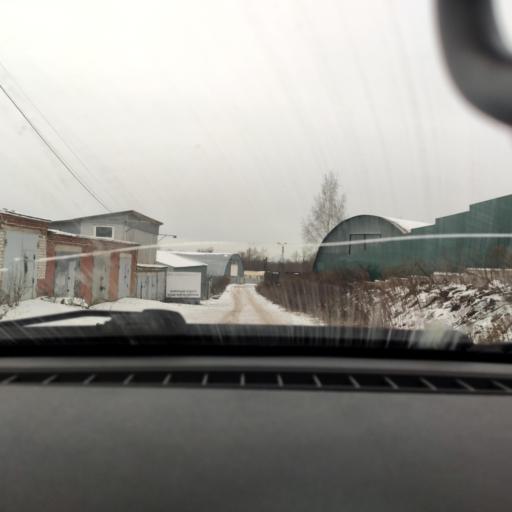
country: RU
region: Bashkortostan
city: Ufa
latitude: 54.8313
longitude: 56.0800
